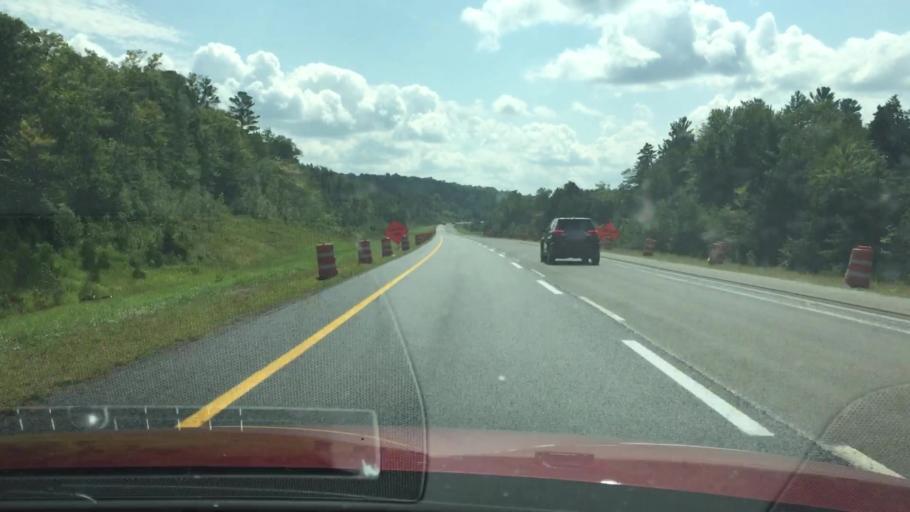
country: US
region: Maine
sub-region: Penobscot County
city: Medway
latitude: 45.7184
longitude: -68.4755
